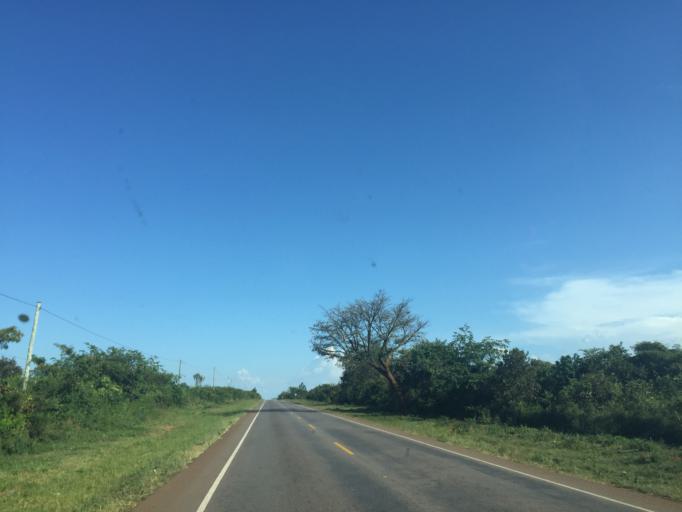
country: UG
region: Central Region
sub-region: Nakasongola District
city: Nakasongola
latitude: 1.3645
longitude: 32.3624
